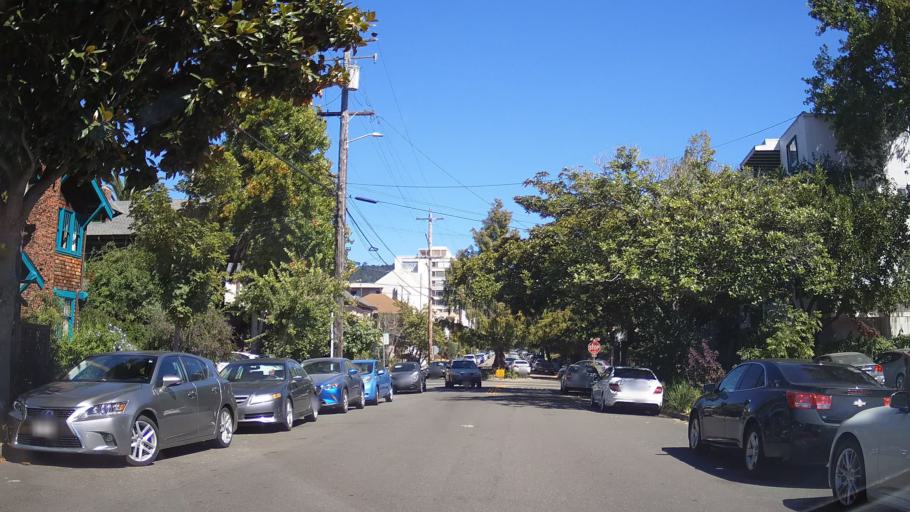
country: US
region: California
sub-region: Alameda County
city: Berkeley
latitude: 37.8626
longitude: -122.2633
